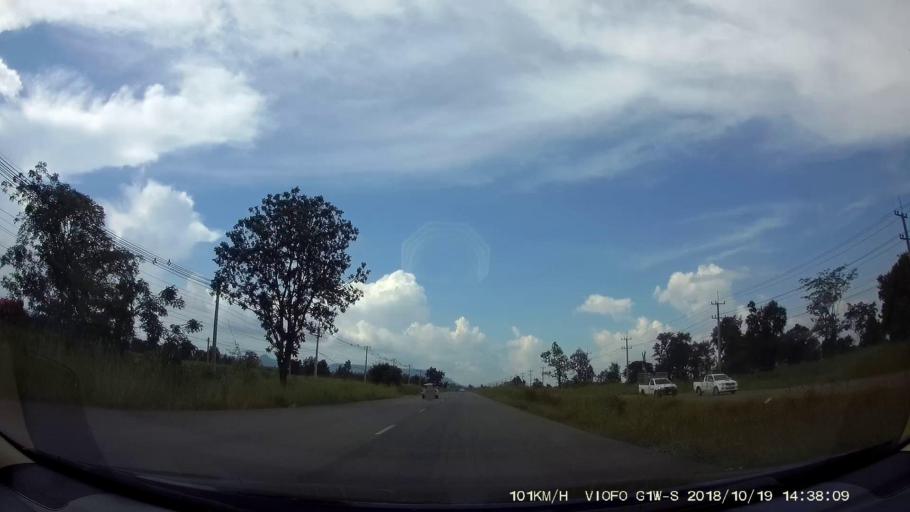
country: TH
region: Chaiyaphum
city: Kaeng Khro
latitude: 16.2067
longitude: 102.2034
